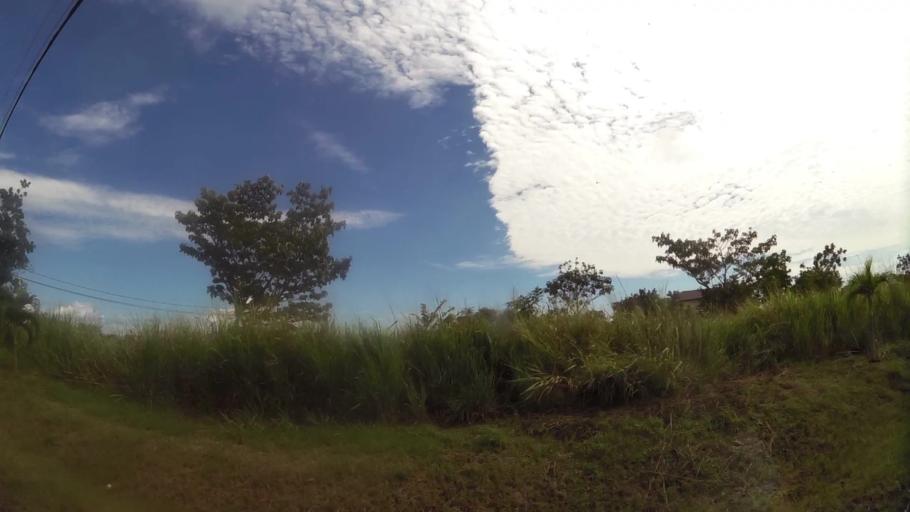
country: PA
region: Panama
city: Nueva Gorgona
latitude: 8.5444
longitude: -79.8989
